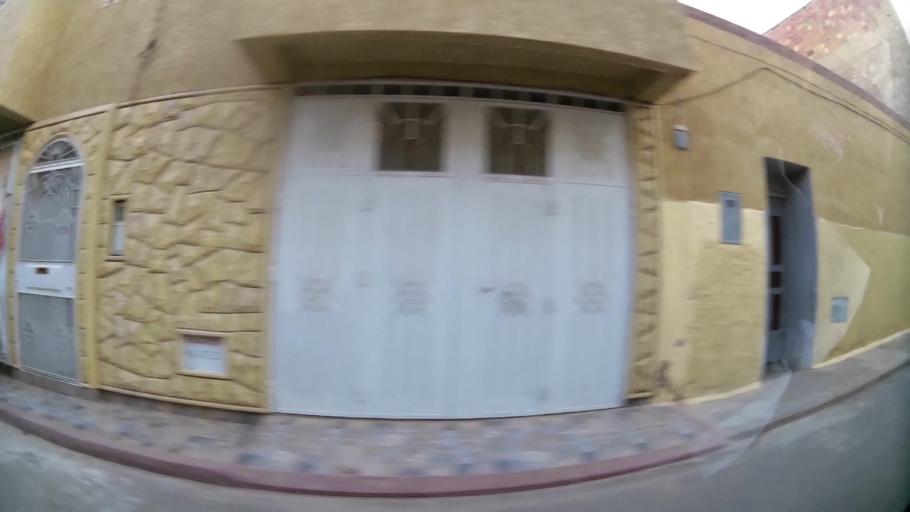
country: MA
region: Oriental
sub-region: Oujda-Angad
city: Oujda
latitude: 34.6992
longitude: -1.9213
